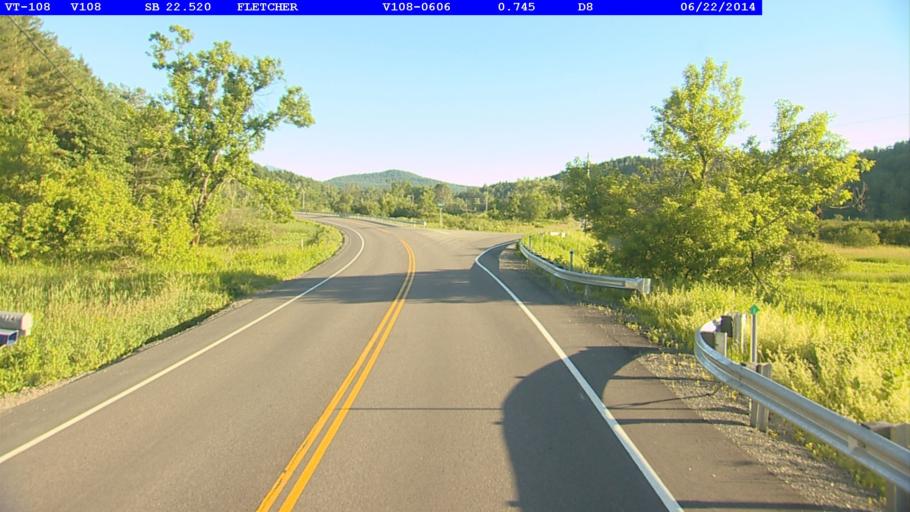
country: US
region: Vermont
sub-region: Lamoille County
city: Johnson
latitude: 44.7127
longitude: -72.8385
